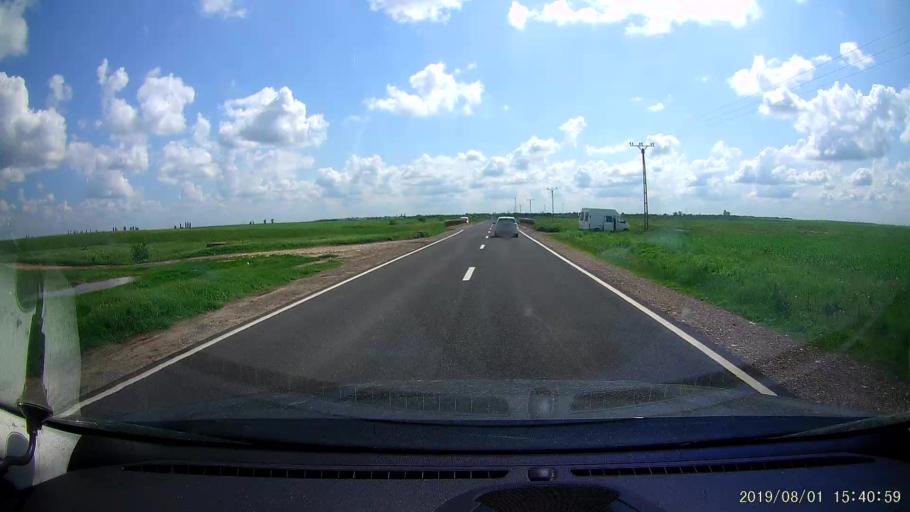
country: RO
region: Braila
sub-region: Comuna Baraganul
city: Baraganul
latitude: 44.8291
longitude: 27.5338
